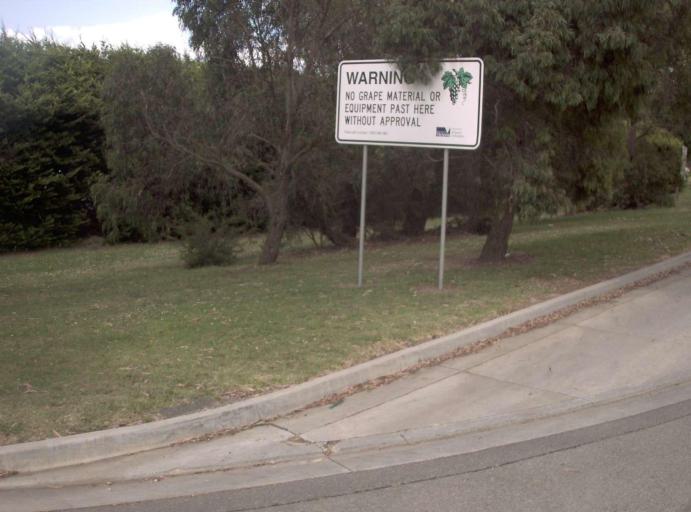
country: AU
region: Victoria
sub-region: Yarra Ranges
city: Lilydale
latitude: -37.7509
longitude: 145.3713
